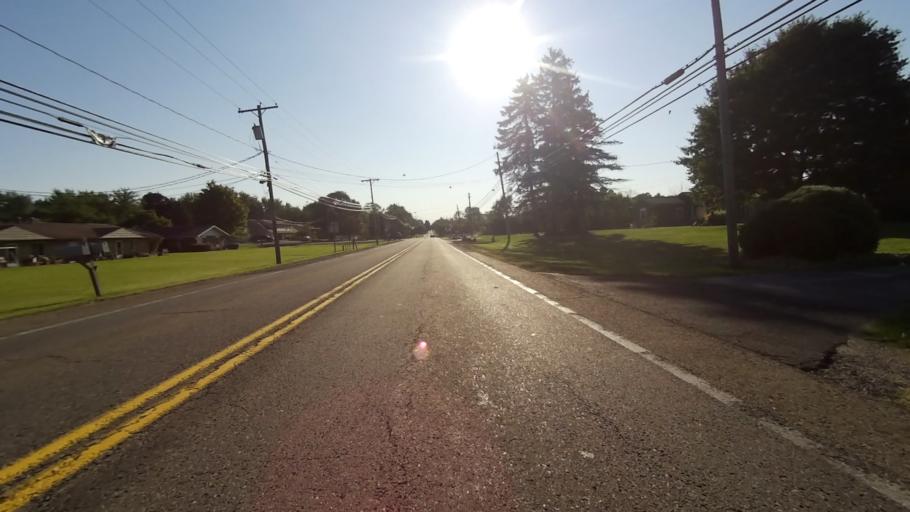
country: US
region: Ohio
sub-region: Portage County
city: Streetsboro
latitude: 41.2390
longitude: -81.3279
